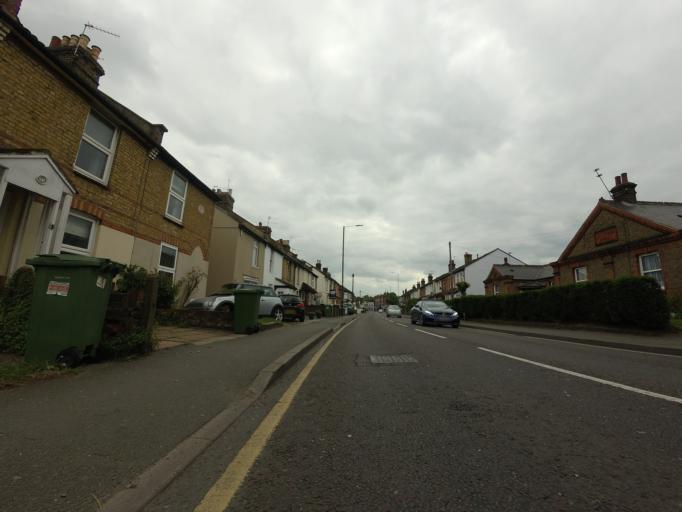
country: GB
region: England
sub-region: Greater London
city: Bexley
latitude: 51.4439
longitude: 0.1518
